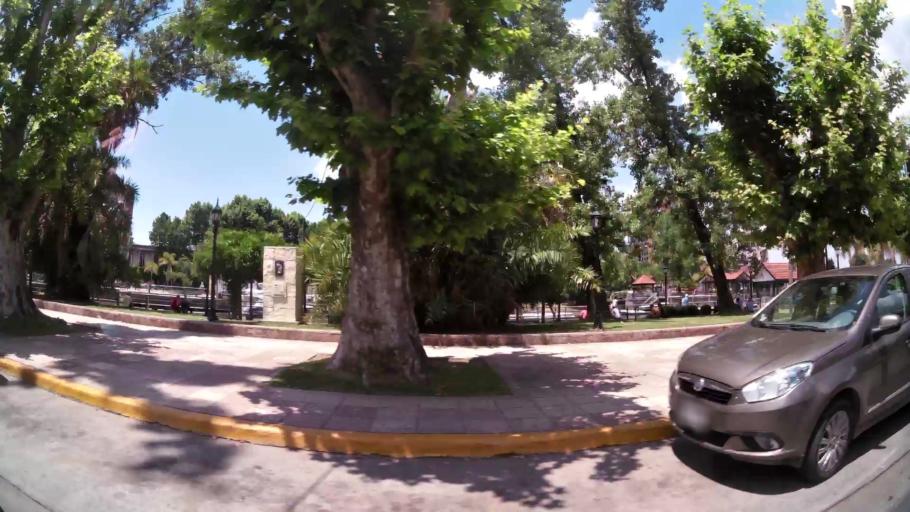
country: AR
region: Buenos Aires
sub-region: Partido de Tigre
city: Tigre
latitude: -34.4198
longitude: -58.5798
